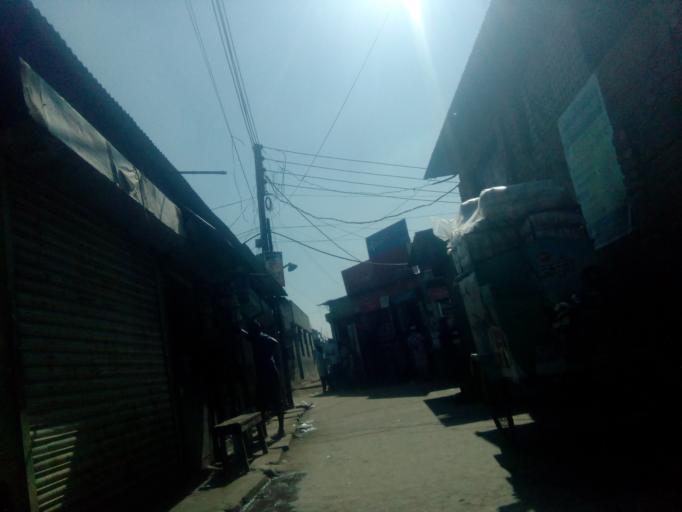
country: BD
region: Dhaka
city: Paltan
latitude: 23.7066
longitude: 90.4749
